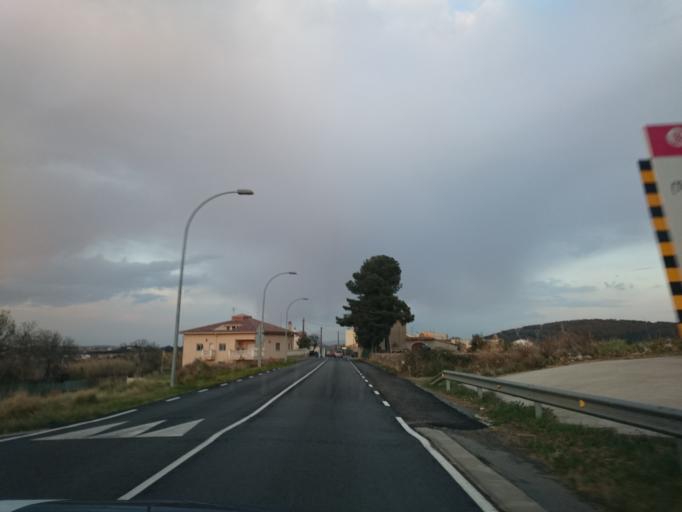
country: ES
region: Catalonia
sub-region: Provincia de Barcelona
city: Sant Marti Sarroca
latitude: 41.3844
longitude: 1.5833
